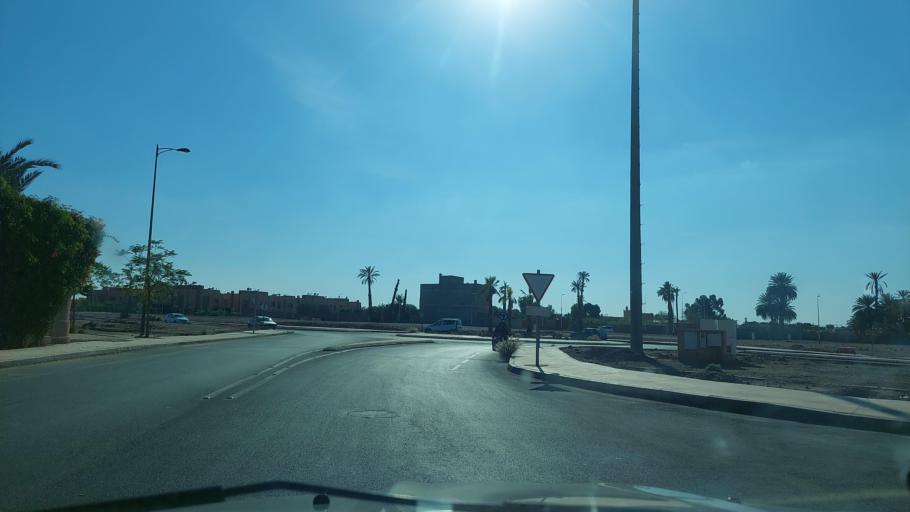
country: MA
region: Marrakech-Tensift-Al Haouz
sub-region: Marrakech
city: Marrakesh
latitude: 31.6590
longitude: -8.0653
